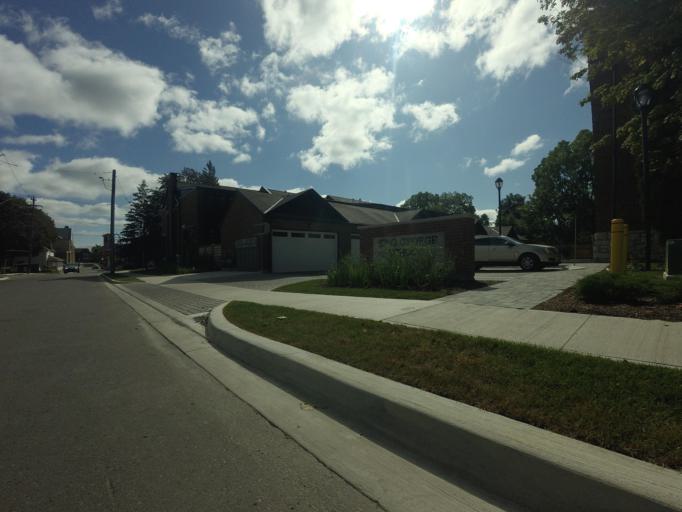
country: CA
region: Ontario
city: Newmarket
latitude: 44.0532
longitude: -79.4606
